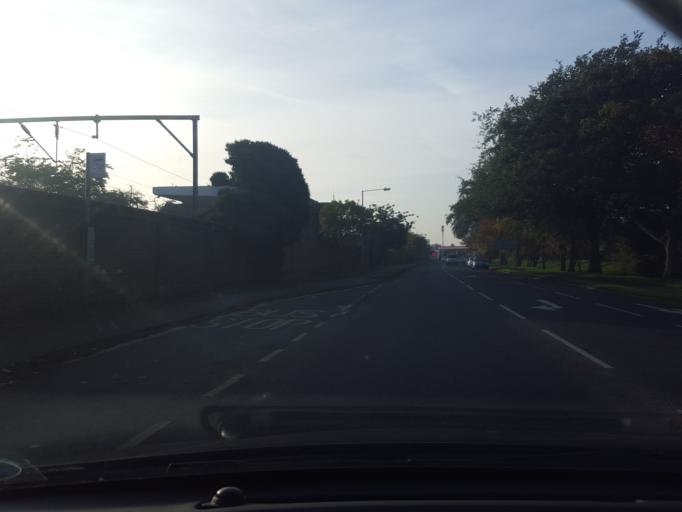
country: GB
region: England
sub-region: Essex
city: Frinton-on-Sea
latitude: 51.8379
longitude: 1.2435
